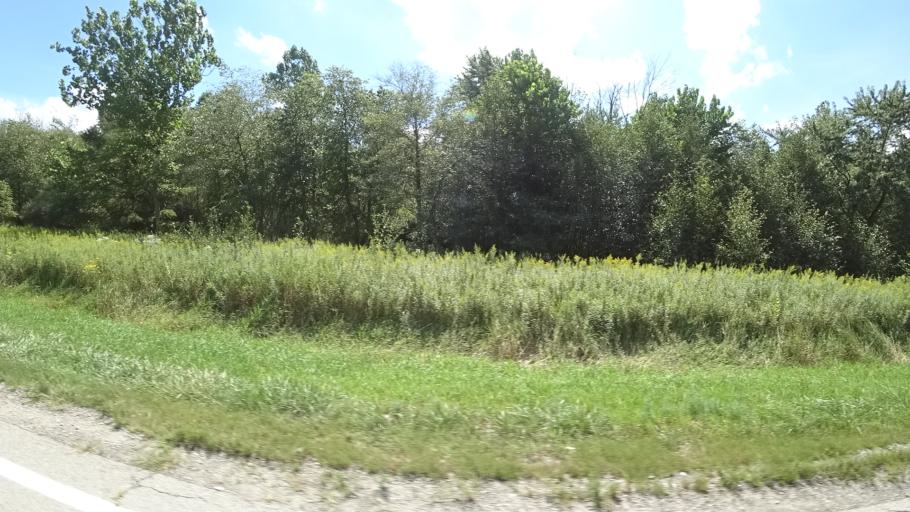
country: US
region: Illinois
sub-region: Cook County
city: Tinley Park
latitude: 41.5570
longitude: -87.7554
